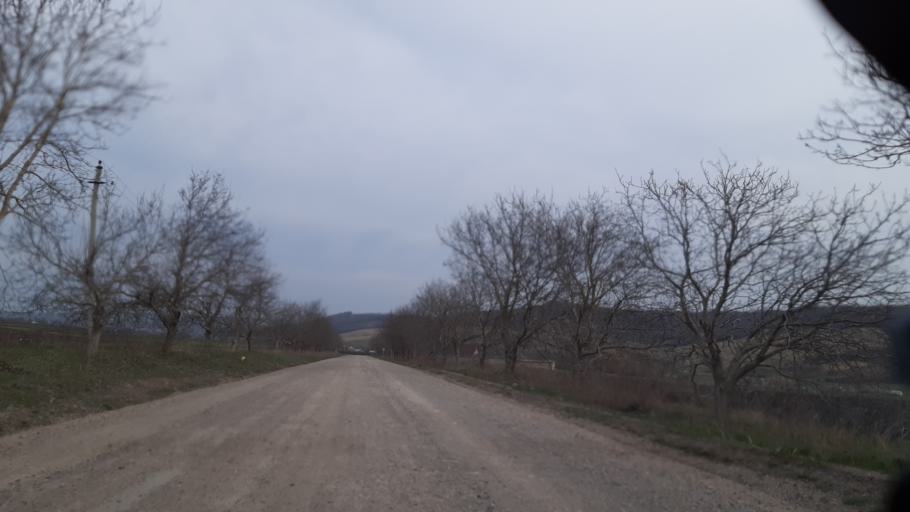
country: MD
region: Soldanesti
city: Soldanesti
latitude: 47.6905
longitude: 28.7409
